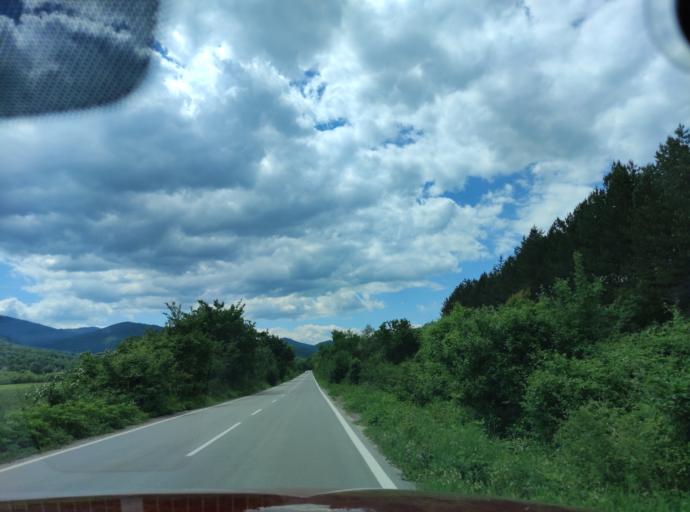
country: BG
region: Montana
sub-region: Obshtina Chiprovtsi
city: Chiprovtsi
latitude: 43.4356
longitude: 22.9547
